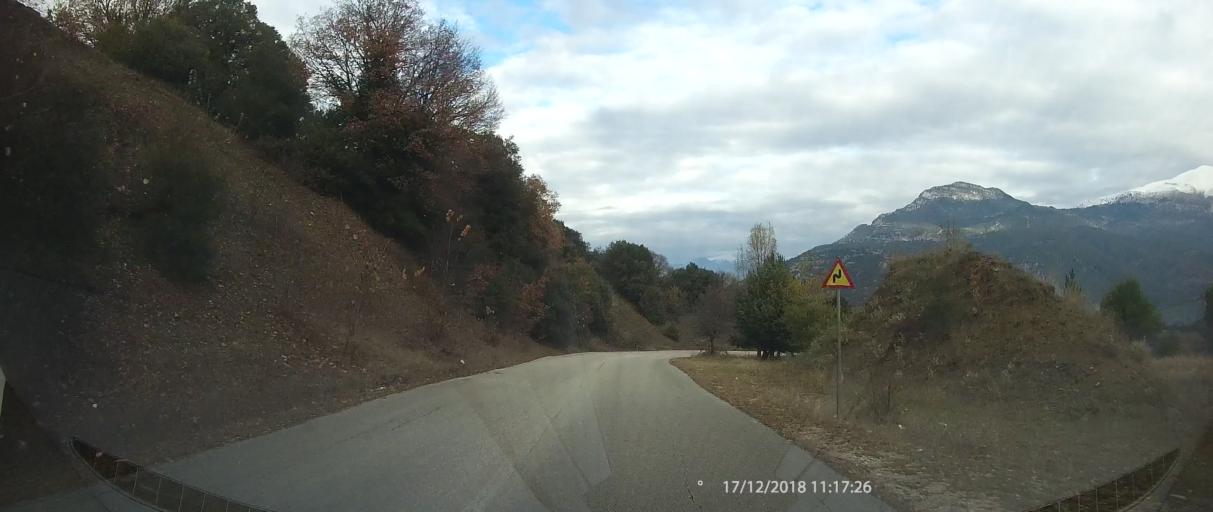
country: GR
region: Epirus
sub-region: Nomos Ioanninon
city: Kalpaki
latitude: 39.9451
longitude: 20.6631
